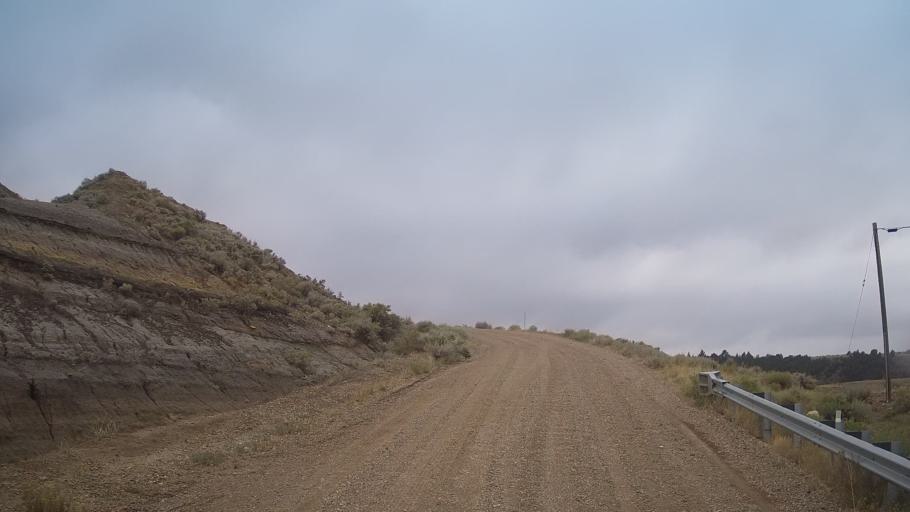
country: US
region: Montana
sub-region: Dawson County
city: Glendive
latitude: 47.0502
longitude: -104.6789
